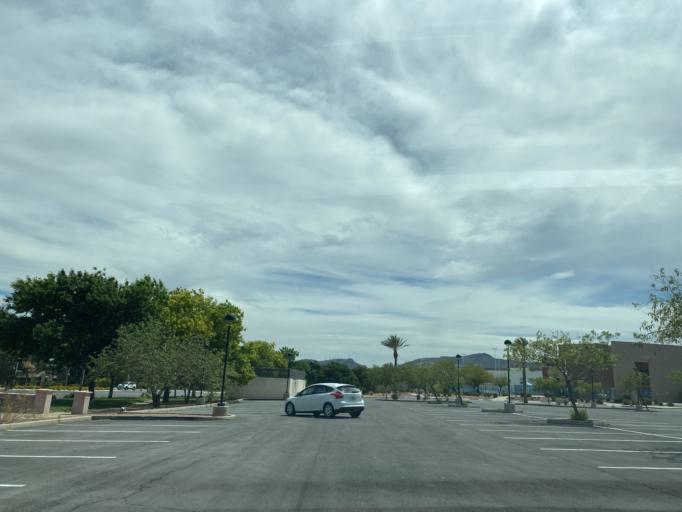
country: US
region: Nevada
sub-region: Clark County
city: Whitney
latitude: 36.0203
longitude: -115.0808
